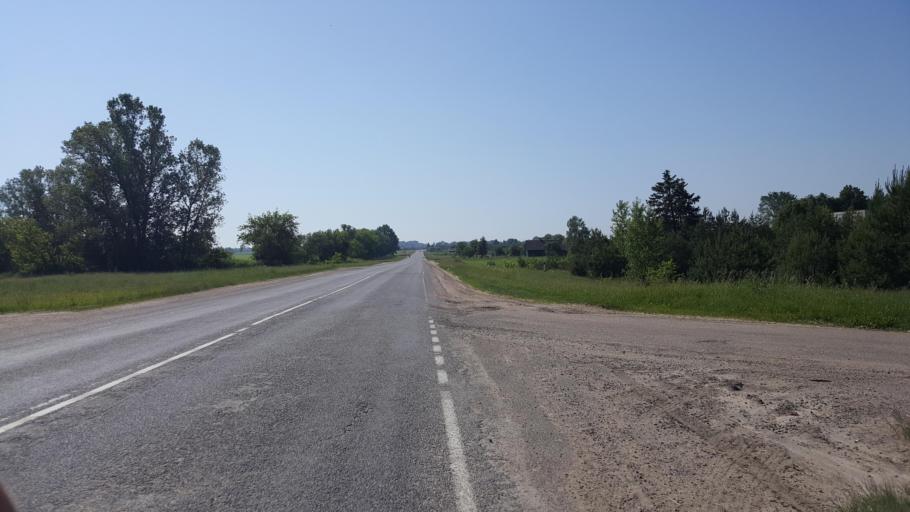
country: BY
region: Brest
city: Kamyanyets
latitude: 52.3364
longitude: 23.9103
